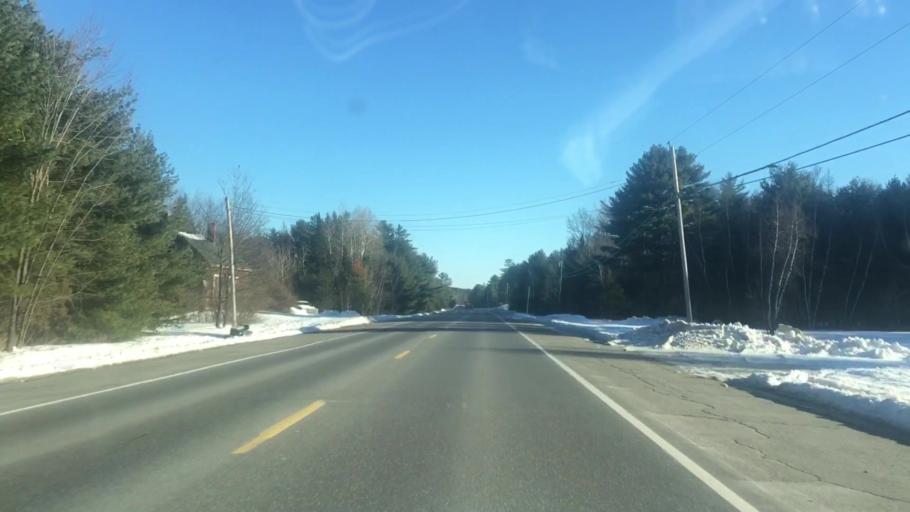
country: US
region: Maine
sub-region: Somerset County
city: Norridgewock
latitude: 44.6924
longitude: -69.7449
